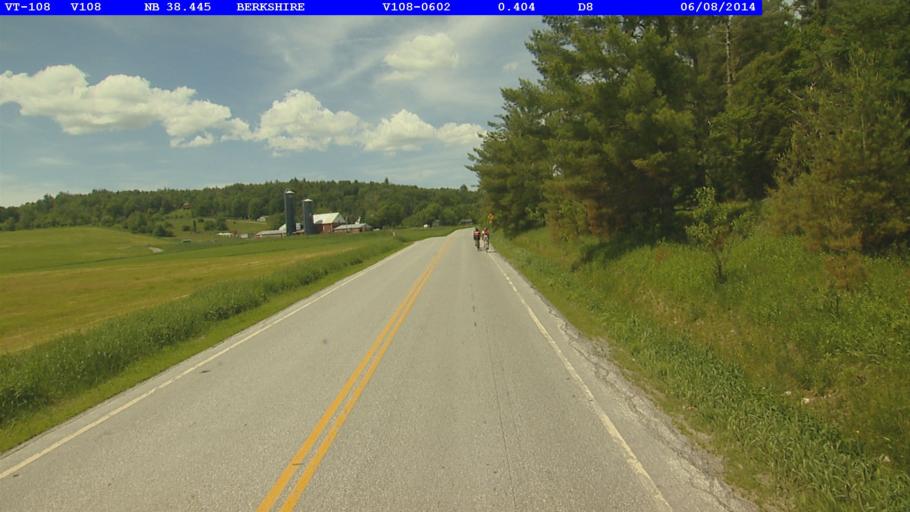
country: US
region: Vermont
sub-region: Franklin County
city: Enosburg Falls
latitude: 44.9306
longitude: -72.8110
